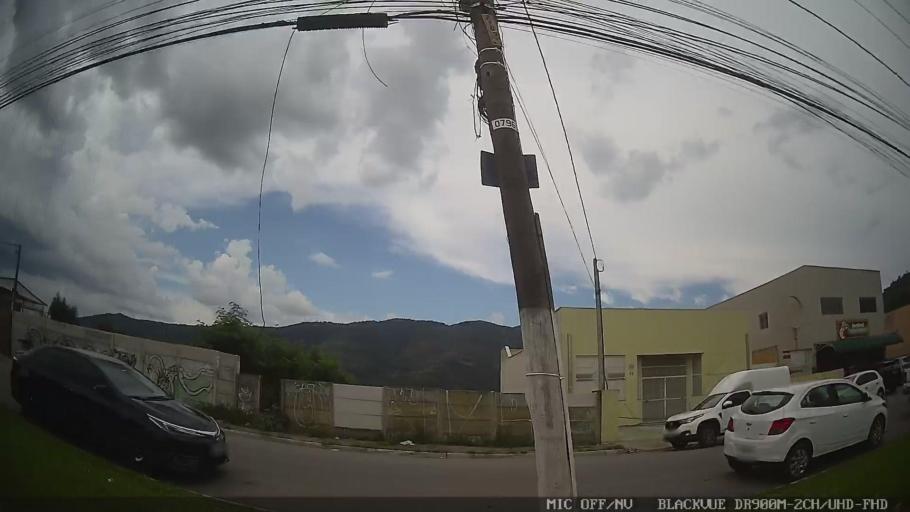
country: BR
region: Sao Paulo
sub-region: Atibaia
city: Atibaia
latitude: -23.1490
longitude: -46.5551
